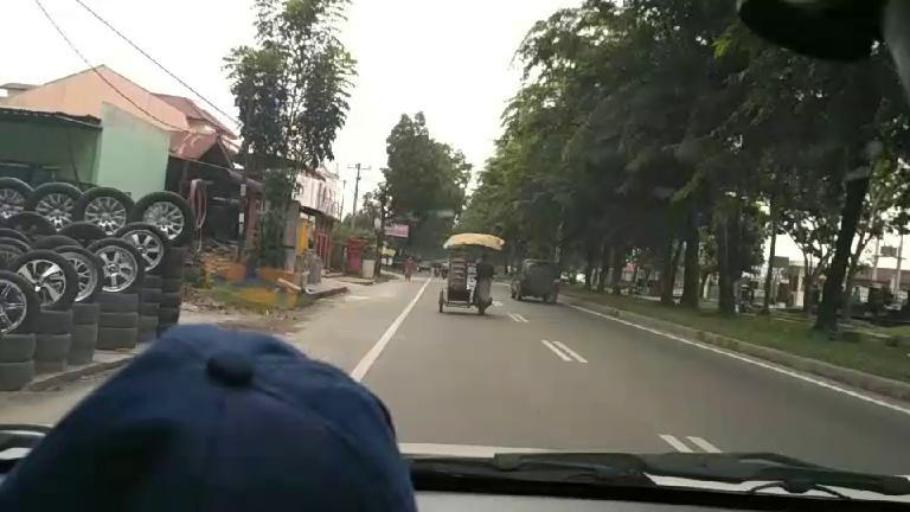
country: ID
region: North Sumatra
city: Sunggal
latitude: 3.5406
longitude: 98.6425
